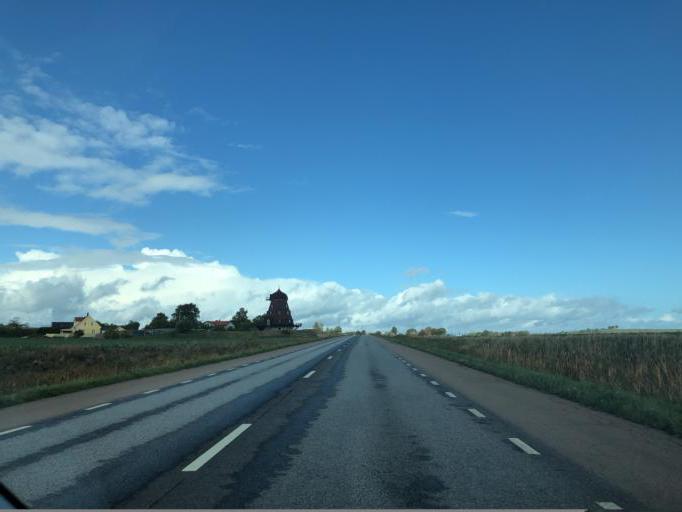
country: SE
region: Skane
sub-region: Landskrona
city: Landskrona
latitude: 55.9101
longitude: 12.8263
